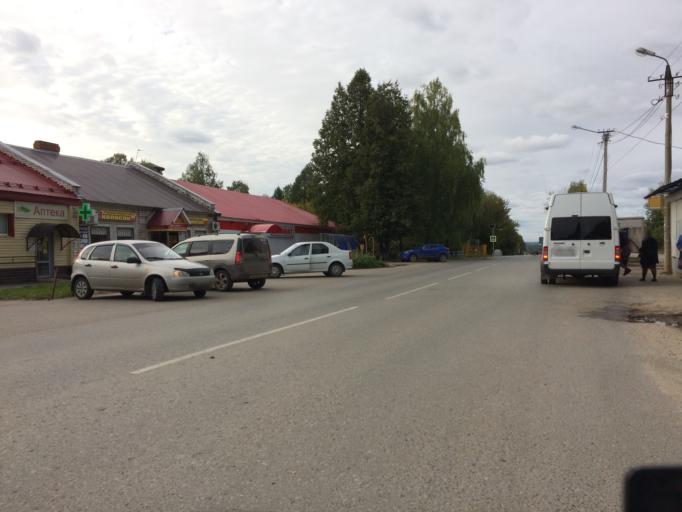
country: RU
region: Mariy-El
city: Yoshkar-Ola
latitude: 56.6541
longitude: 47.9773
